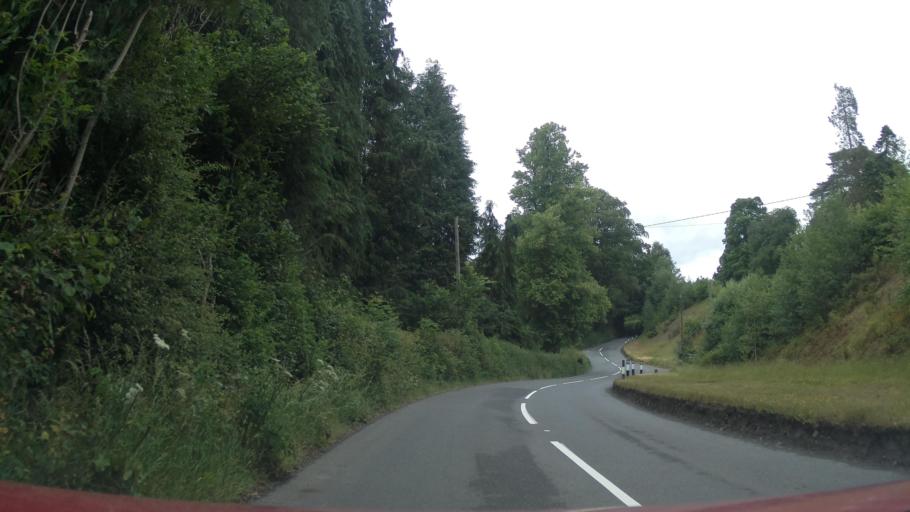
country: GB
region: England
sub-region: Devon
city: Crediton
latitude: 50.6973
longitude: -3.6345
